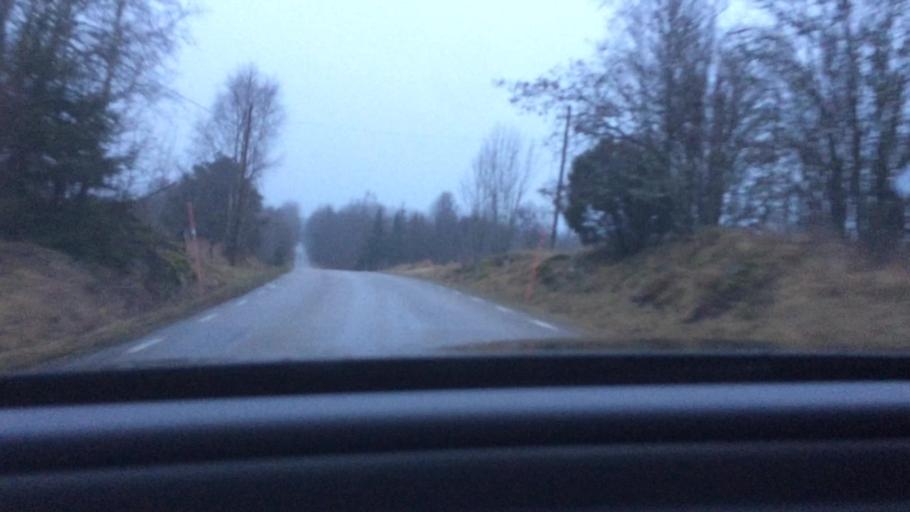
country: SE
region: Vaestra Goetaland
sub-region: Ulricehamns Kommun
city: Ulricehamn
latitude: 57.9580
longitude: 13.3946
